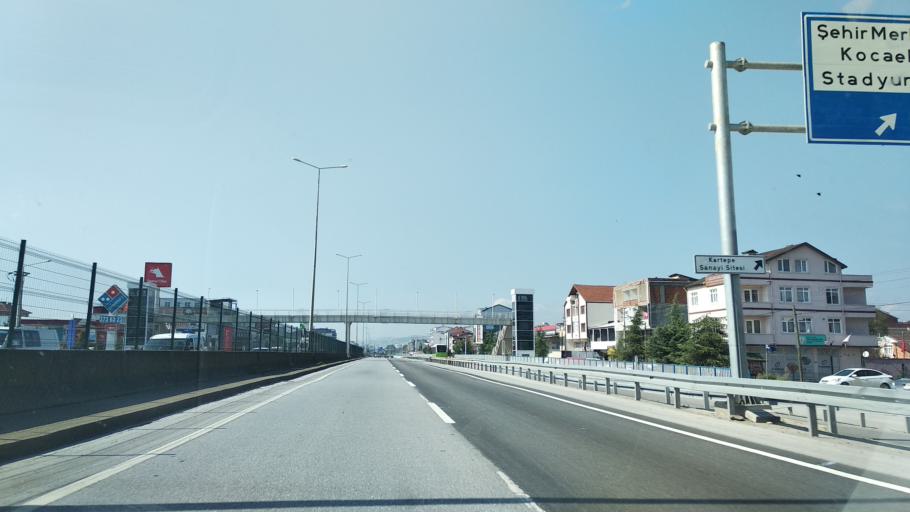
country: TR
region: Kocaeli
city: Kosekoy
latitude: 40.7525
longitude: 30.0298
